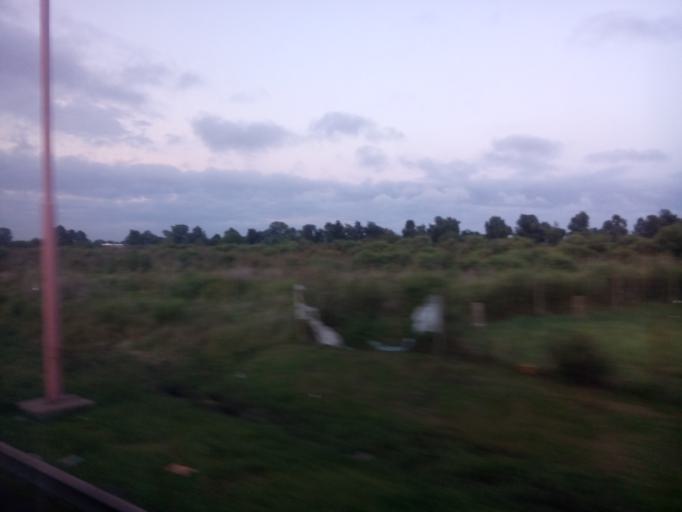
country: AR
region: Buenos Aires
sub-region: Partido de Zarate
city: Zarate
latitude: -34.1188
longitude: -59.0124
